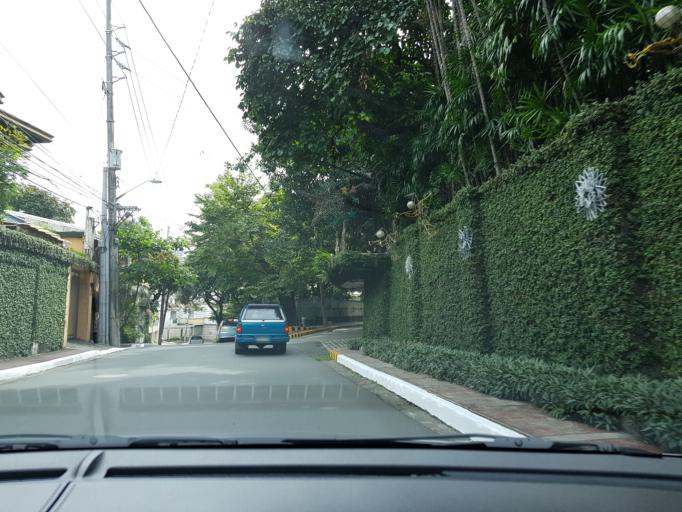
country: PH
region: Metro Manila
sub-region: San Juan
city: San Juan
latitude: 14.6117
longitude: 121.0404
